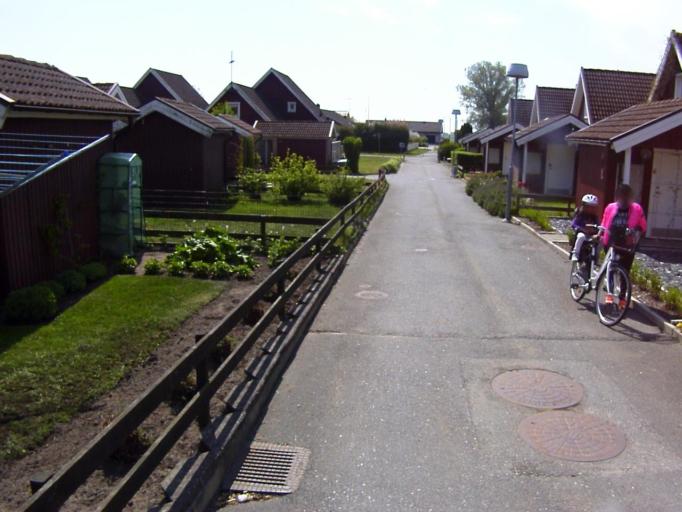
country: SE
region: Skane
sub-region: Kristianstads Kommun
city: Fjalkinge
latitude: 56.0427
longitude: 14.2682
